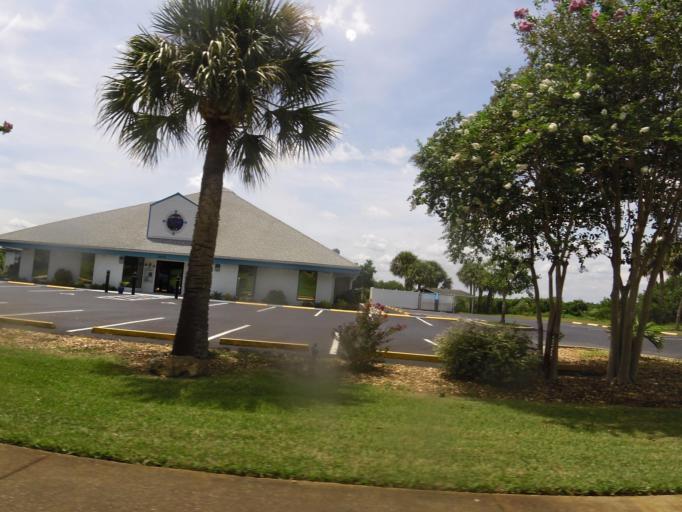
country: US
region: Florida
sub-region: Volusia County
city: Ponce Inlet
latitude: 29.0996
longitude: -80.9411
